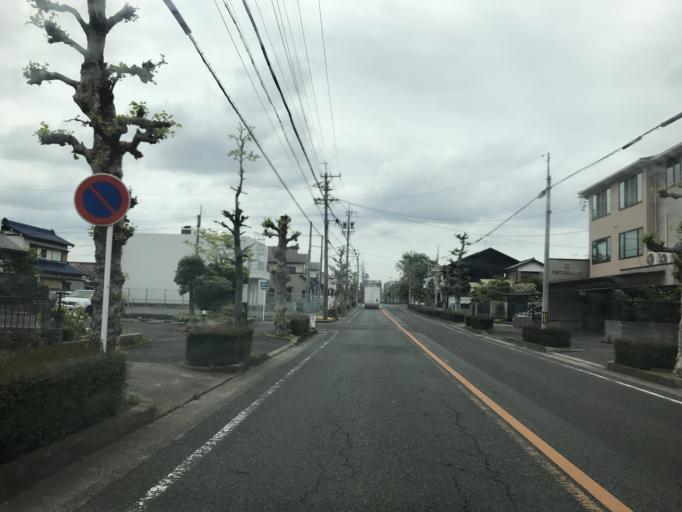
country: JP
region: Aichi
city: Kasugai
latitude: 35.2403
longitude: 136.9749
